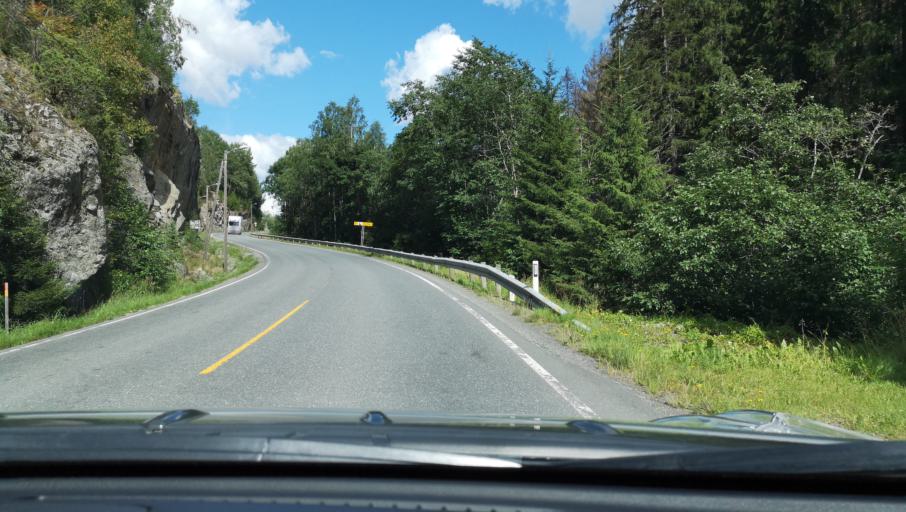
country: NO
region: Ostfold
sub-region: Hobol
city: Tomter
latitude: 59.6533
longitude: 10.9990
